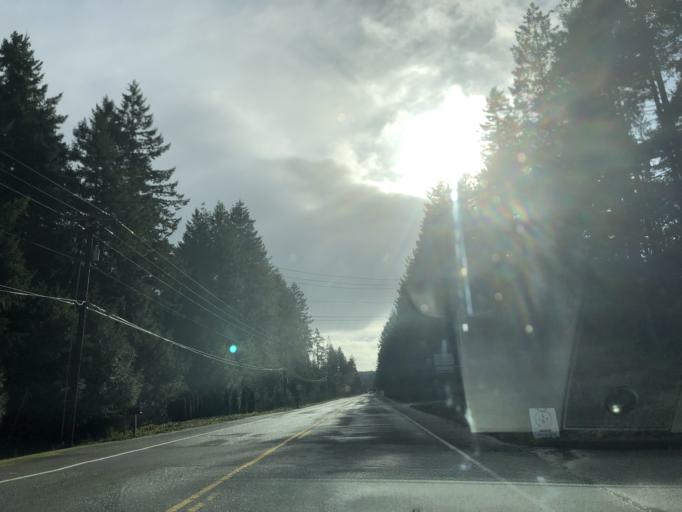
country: US
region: Washington
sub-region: Kitsap County
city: Poulsbo
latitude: 47.7641
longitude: -122.6507
